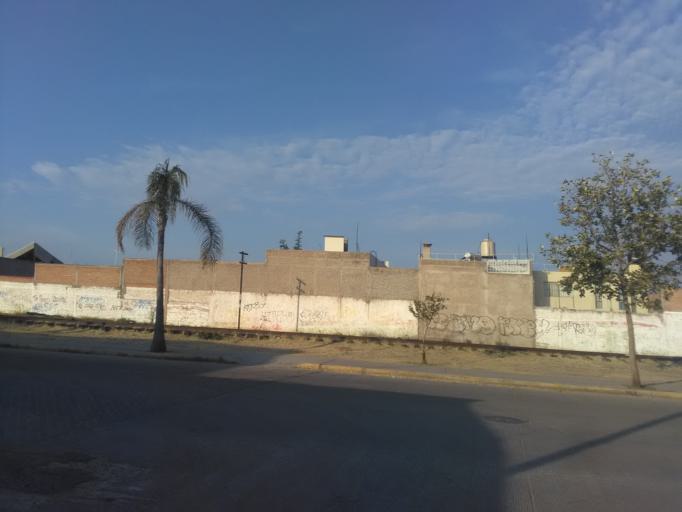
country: MX
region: Durango
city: Victoria de Durango
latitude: 24.0449
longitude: -104.6529
